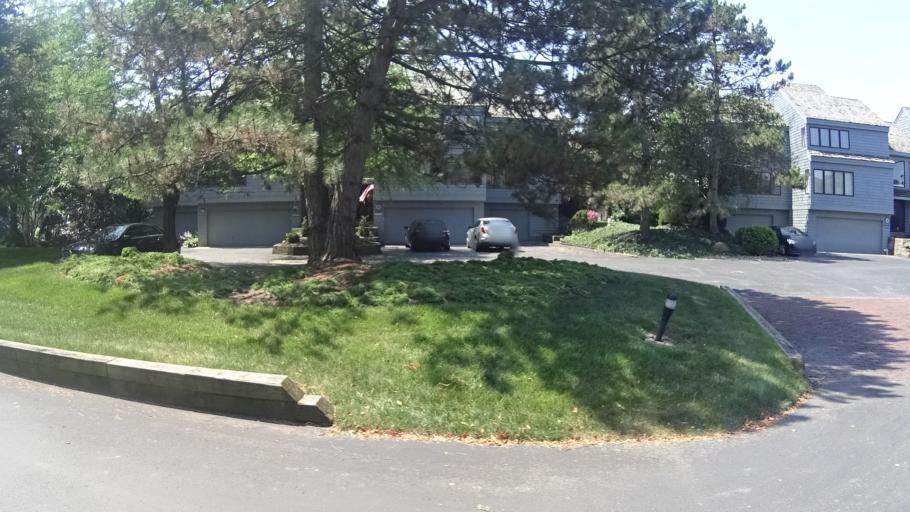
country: US
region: Ohio
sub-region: Erie County
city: Huron
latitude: 41.4126
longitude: -82.5938
